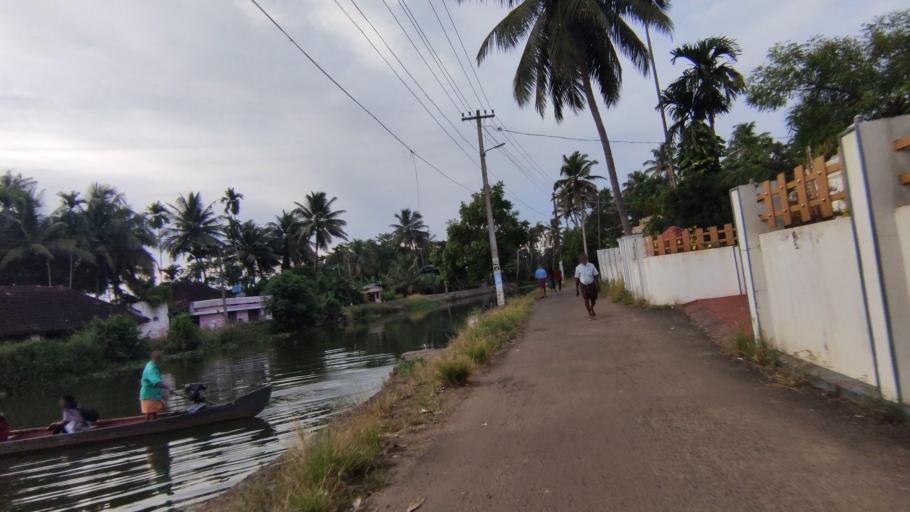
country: IN
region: Kerala
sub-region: Kottayam
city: Kottayam
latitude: 9.6449
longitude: 76.4787
